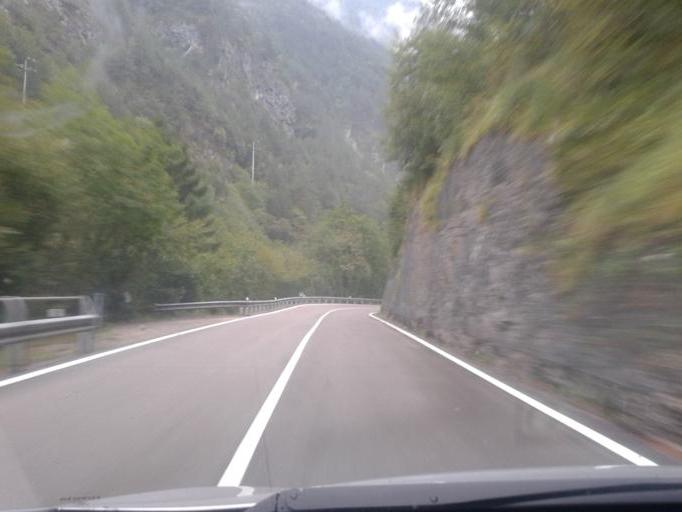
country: IT
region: Trentino-Alto Adige
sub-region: Provincia di Trento
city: Storo
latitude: 45.8440
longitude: 10.5977
